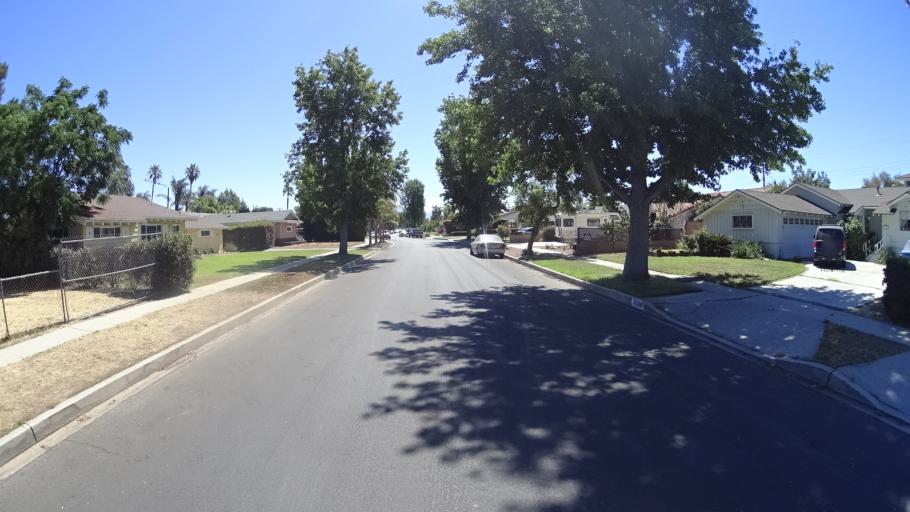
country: US
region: California
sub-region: Los Angeles County
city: San Fernando
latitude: 34.2563
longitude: -118.4643
